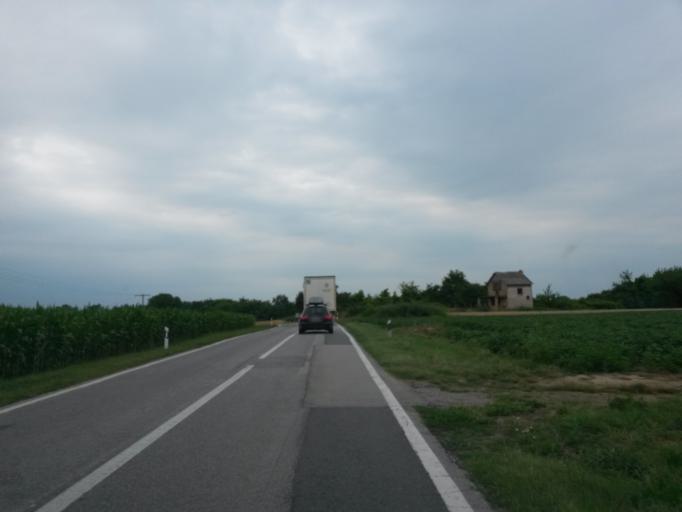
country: HR
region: Vukovarsko-Srijemska
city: Lovas
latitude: 45.2830
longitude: 19.1265
